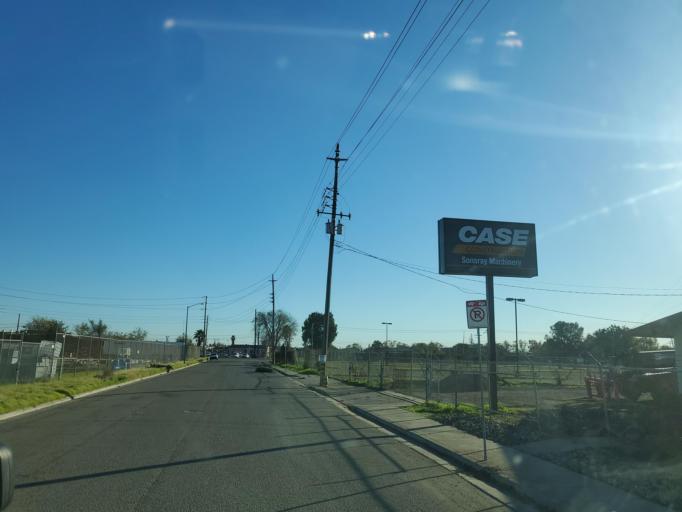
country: US
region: California
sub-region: San Joaquin County
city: Stockton
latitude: 37.9389
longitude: -121.3063
